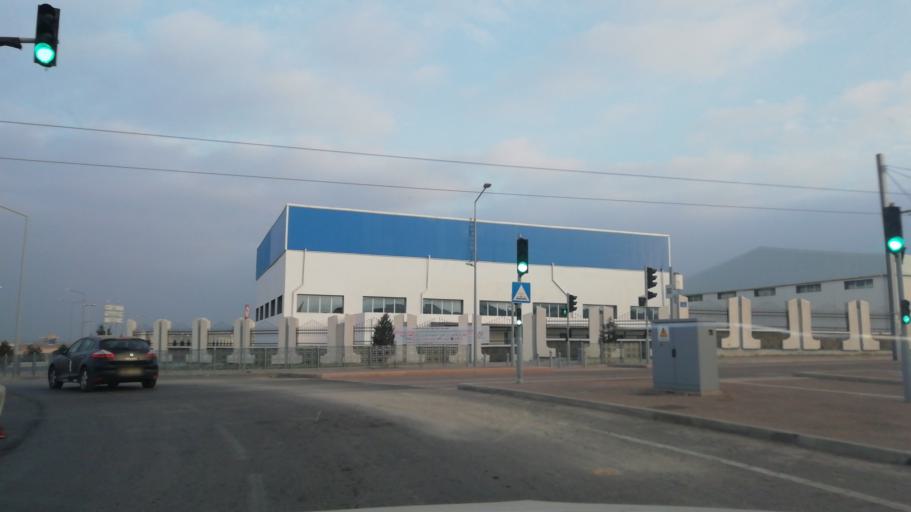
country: DZ
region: Sidi Bel Abbes
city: Sidi Bel Abbes
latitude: 35.2254
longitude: -0.6368
